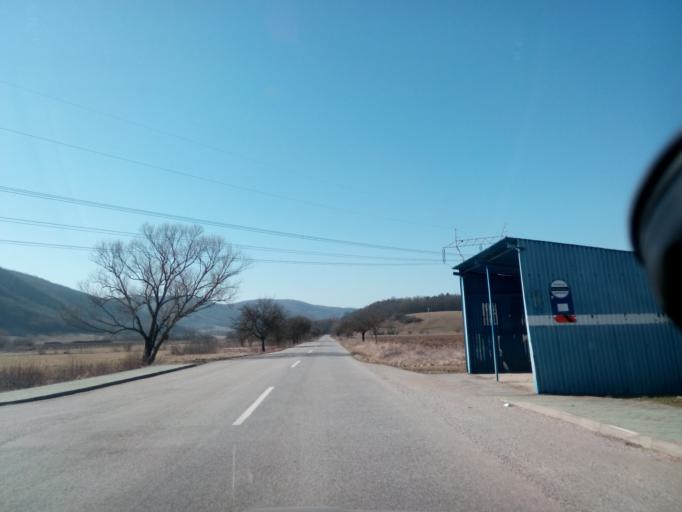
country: SK
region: Kosicky
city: Roznava
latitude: 48.5817
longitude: 20.6580
